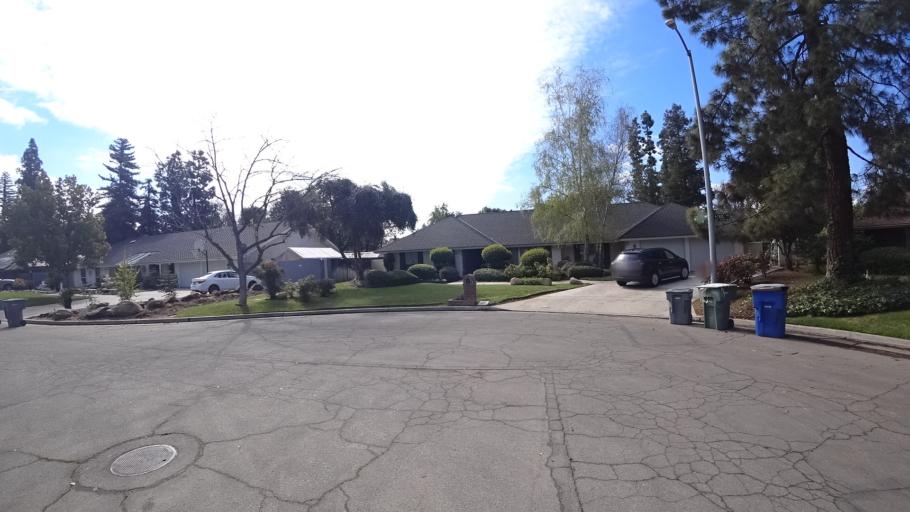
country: US
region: California
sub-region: Fresno County
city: Fresno
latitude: 36.8322
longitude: -119.8463
